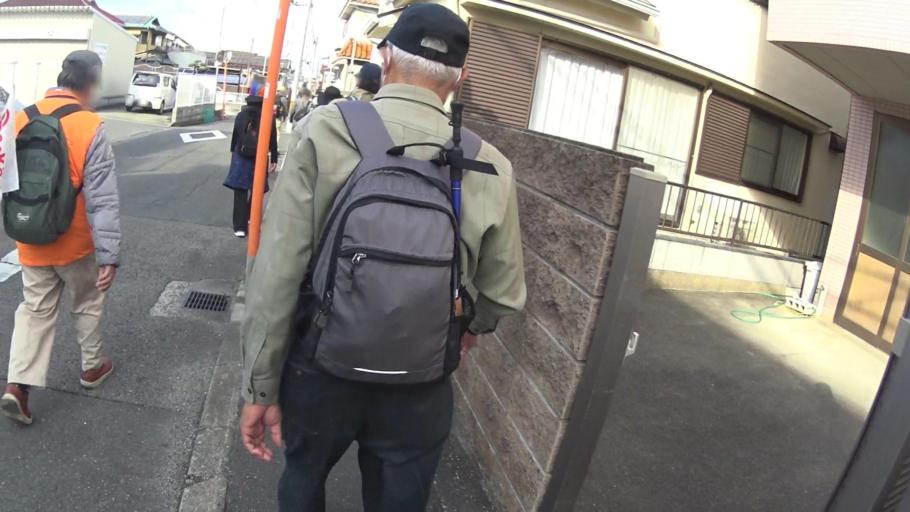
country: JP
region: Osaka
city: Kashihara
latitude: 34.5805
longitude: 135.5911
